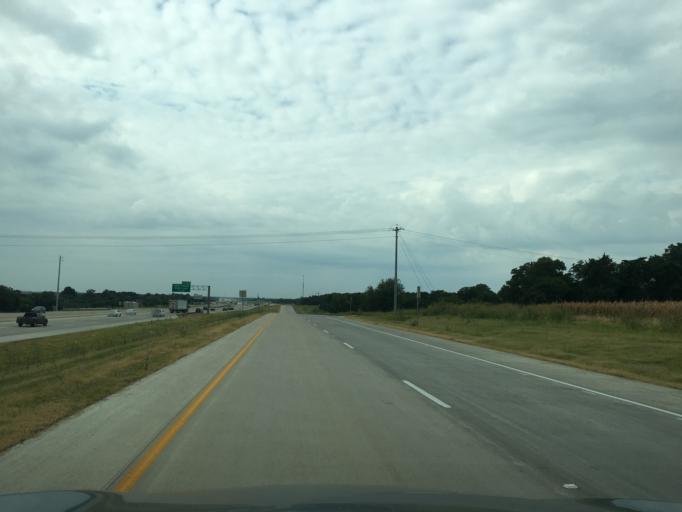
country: US
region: Texas
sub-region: Collin County
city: Anna
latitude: 33.3347
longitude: -96.5890
